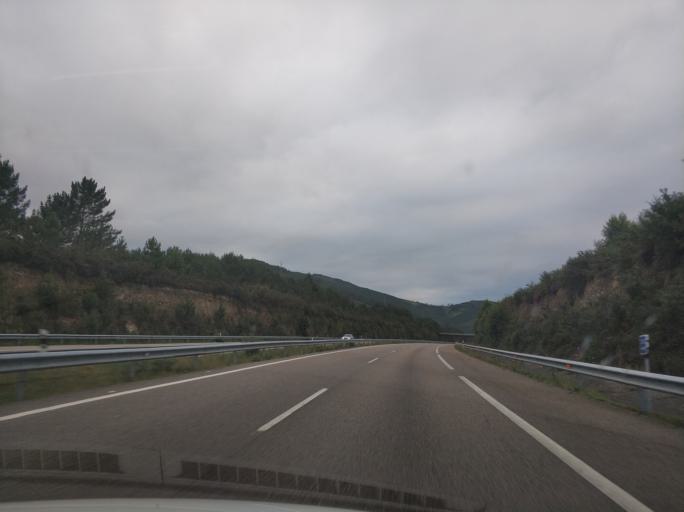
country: ES
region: Asturias
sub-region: Province of Asturias
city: Tineo
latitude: 43.5396
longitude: -6.4769
